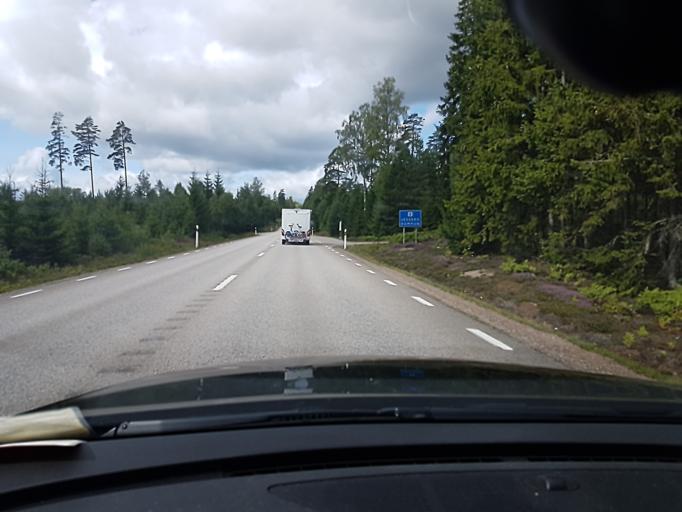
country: SE
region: Kronoberg
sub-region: Lessebo Kommun
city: Lessebo
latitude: 56.7301
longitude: 15.3683
